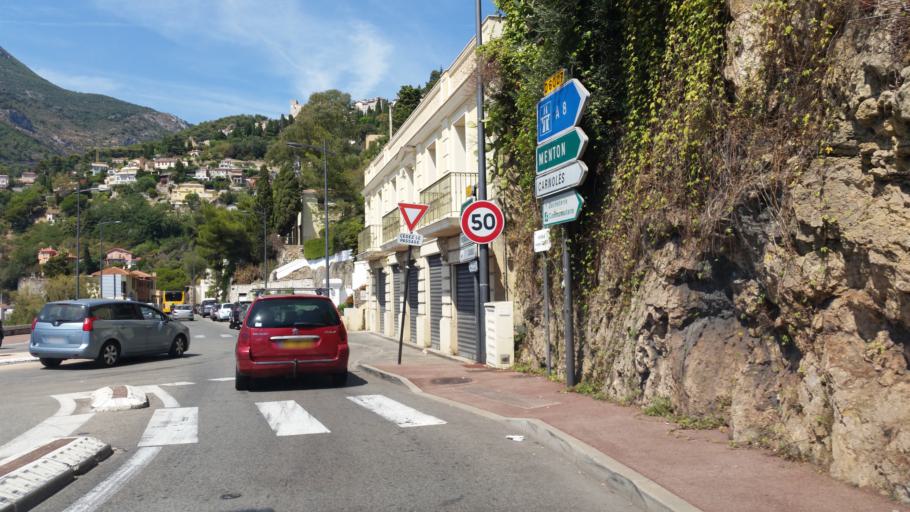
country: FR
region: Provence-Alpes-Cote d'Azur
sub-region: Departement des Alpes-Maritimes
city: Roquebrune-Cap-Martin
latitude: 43.7607
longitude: 7.4647
